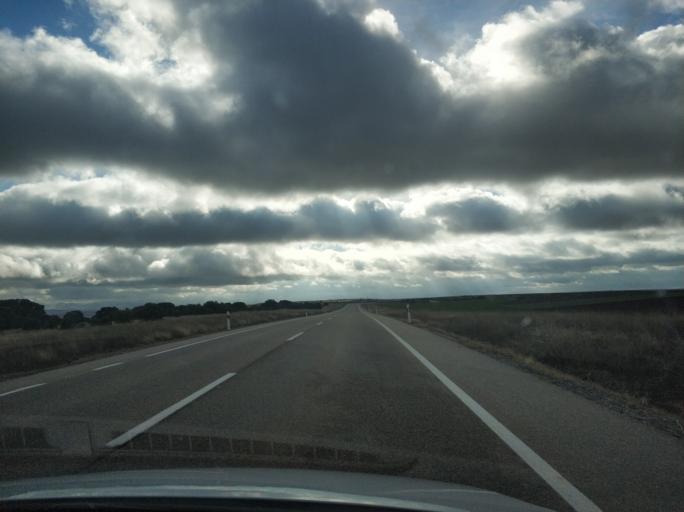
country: ES
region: Castille and Leon
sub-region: Provincia de Soria
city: Fuentecambron
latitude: 41.4809
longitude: -3.3180
